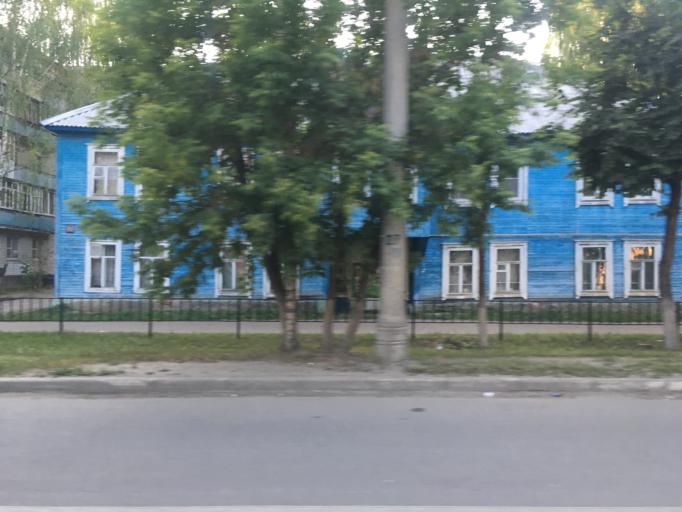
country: RU
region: Mariy-El
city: Yoshkar-Ola
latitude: 56.6444
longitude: 47.8913
